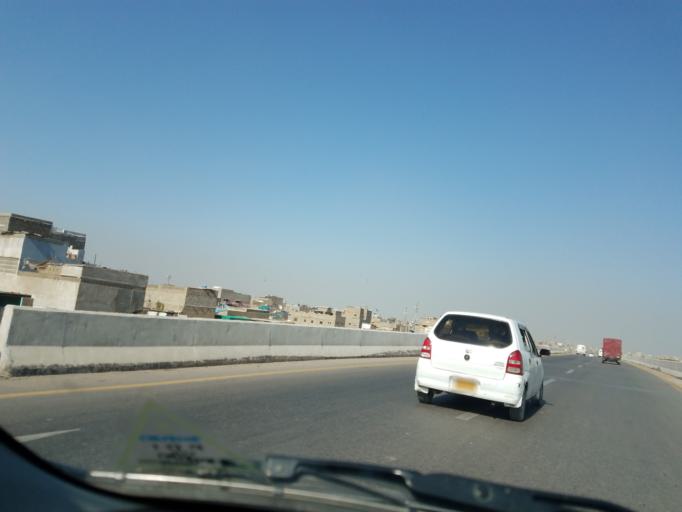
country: PK
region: Sindh
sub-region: Karachi District
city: Karachi
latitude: 24.8841
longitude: 67.0205
